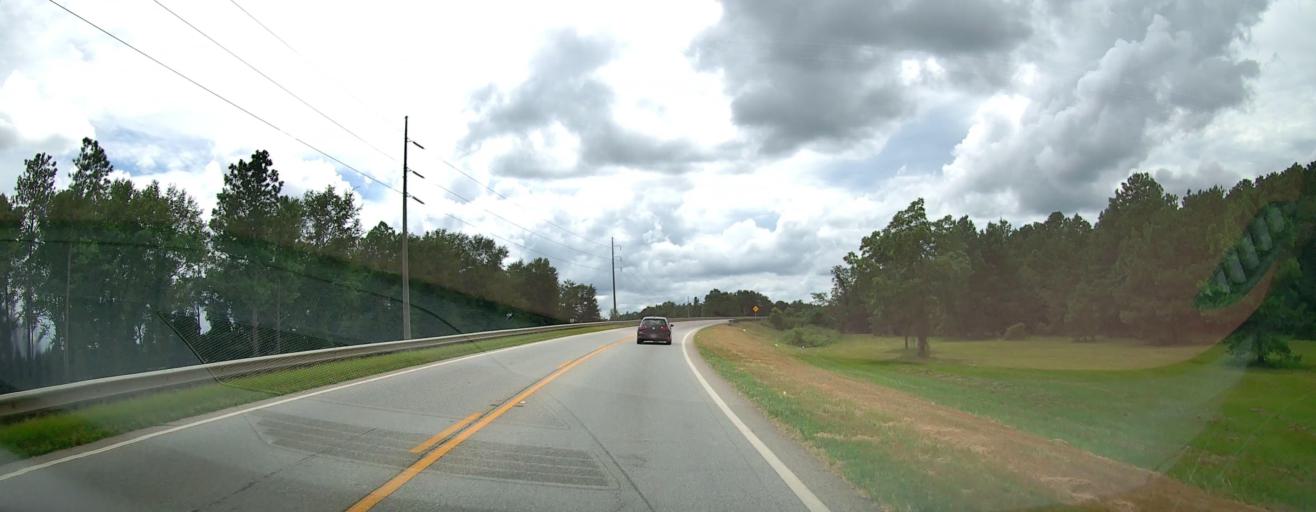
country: US
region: Georgia
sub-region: Macon County
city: Oglethorpe
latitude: 32.2757
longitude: -84.0671
